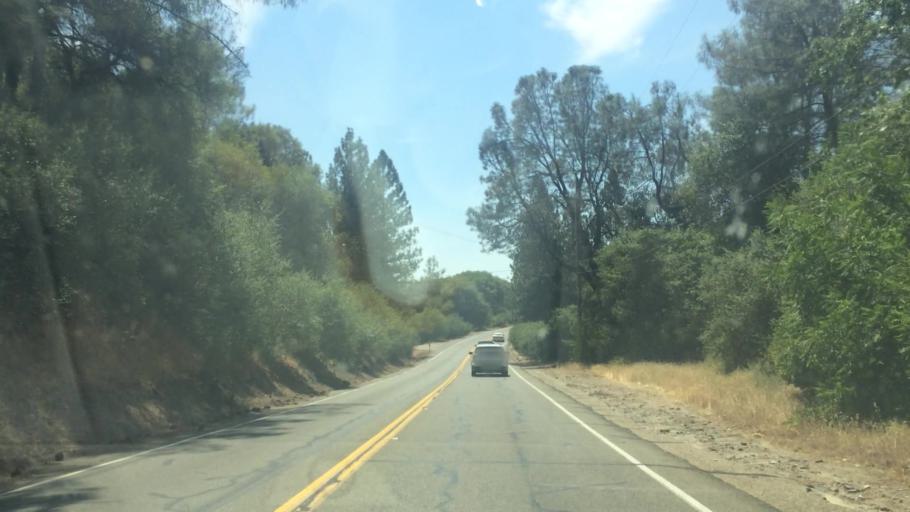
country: US
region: California
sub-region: Amador County
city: Jackson
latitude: 38.3985
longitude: -120.7387
